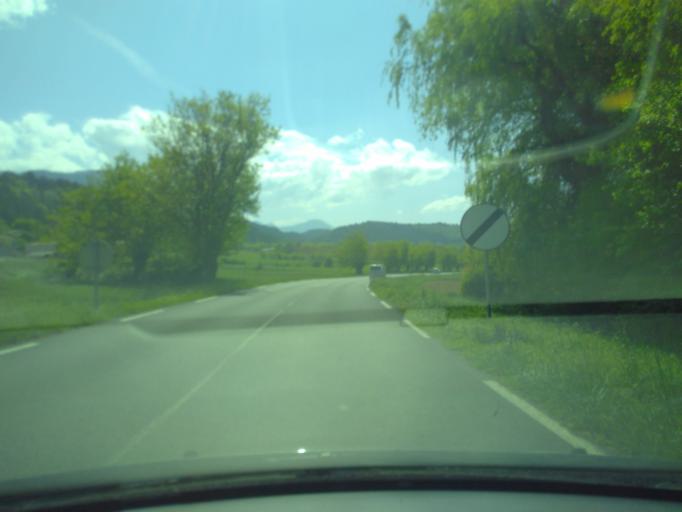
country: FR
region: Rhone-Alpes
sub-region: Departement de la Drome
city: Die
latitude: 44.7256
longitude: 5.3968
